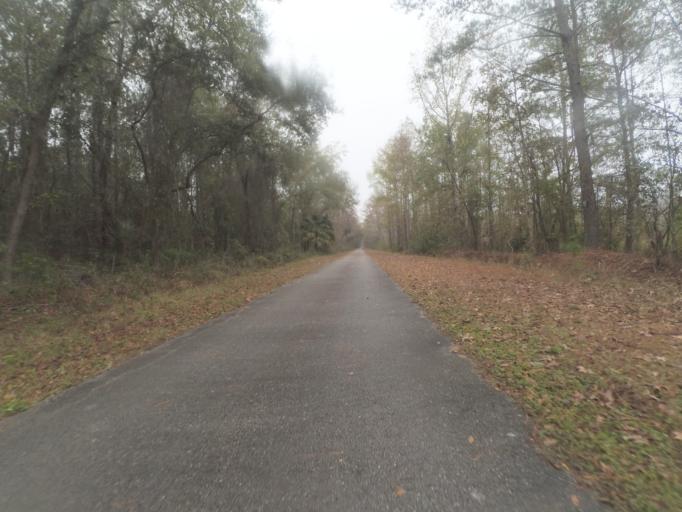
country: US
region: Florida
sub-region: Alachua County
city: Hawthorne
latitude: 29.5962
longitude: -82.1665
